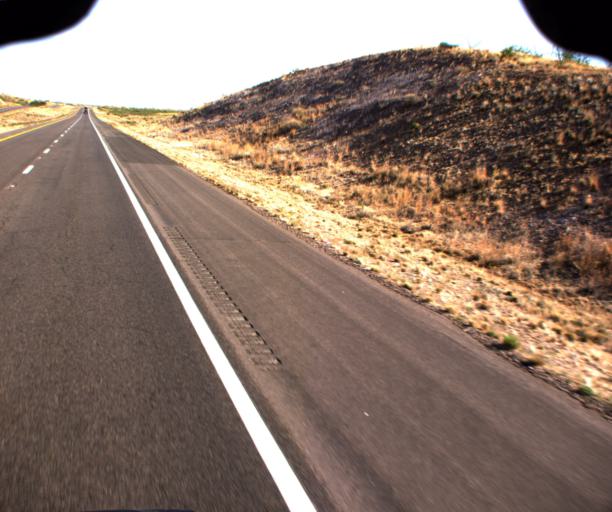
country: US
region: Arizona
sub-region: Graham County
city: Swift Trail Junction
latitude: 32.5089
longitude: -109.6738
